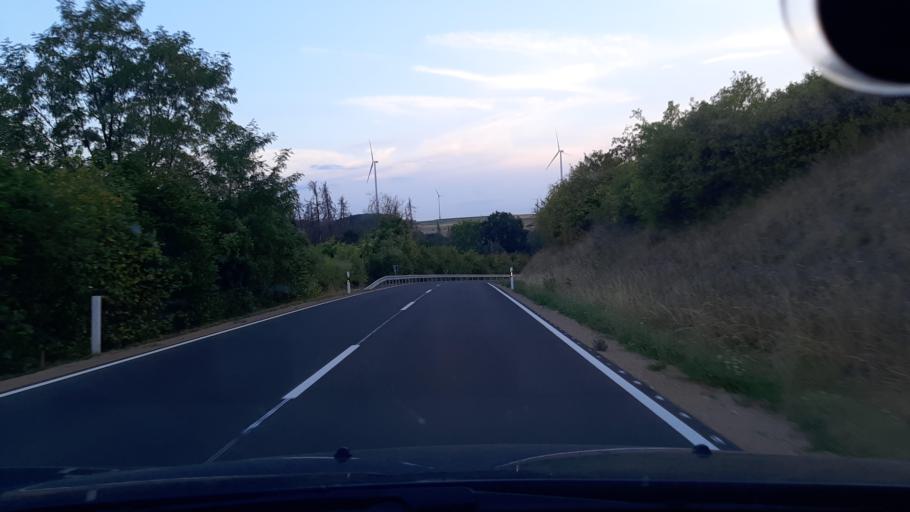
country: DE
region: North Rhine-Westphalia
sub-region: Regierungsbezirk Koln
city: Mechernich
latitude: 50.5574
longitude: 6.6278
